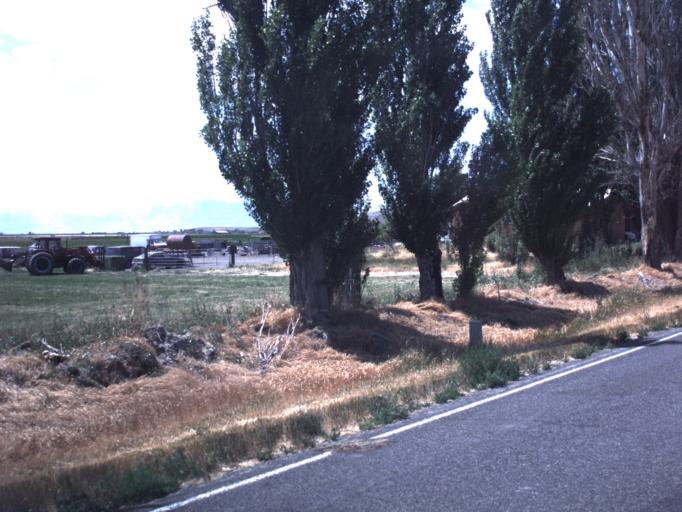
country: US
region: Utah
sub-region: Box Elder County
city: Tremonton
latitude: 41.6508
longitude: -112.3054
